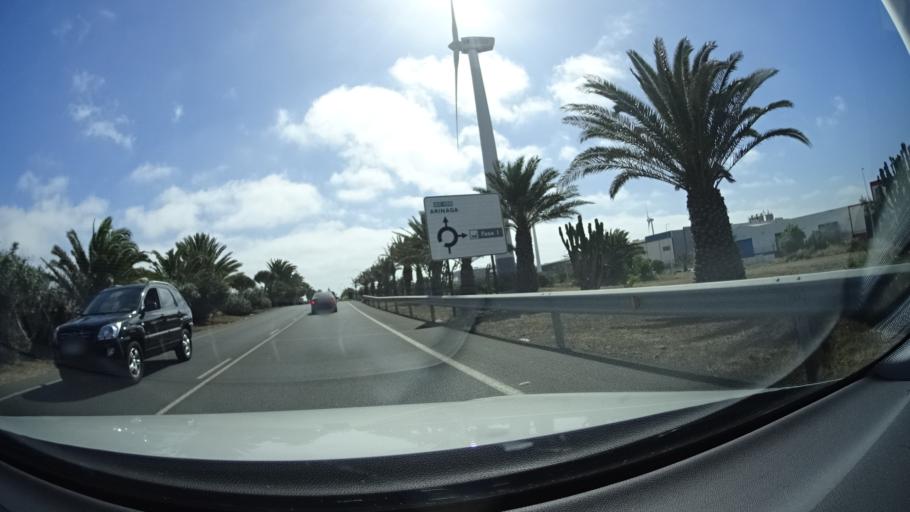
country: ES
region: Canary Islands
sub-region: Provincia de Las Palmas
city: Cruce de Arinaga
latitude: 27.8637
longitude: -15.4069
